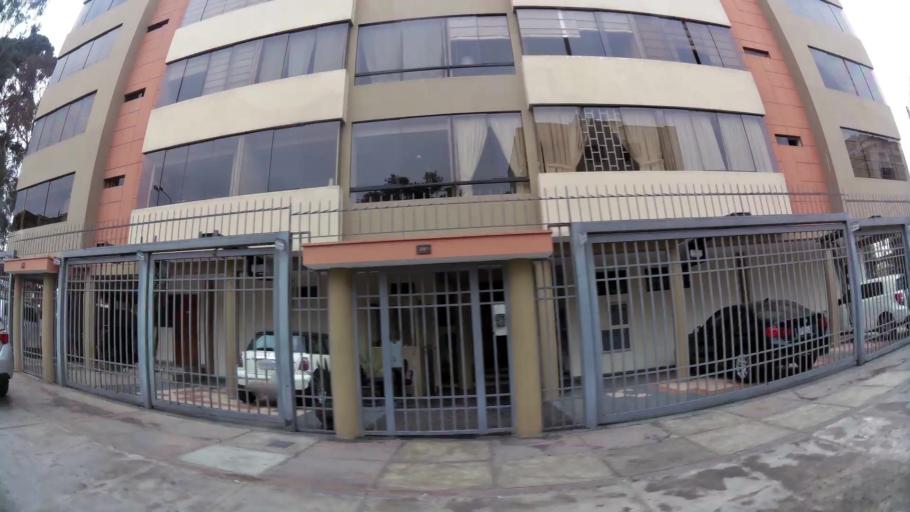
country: PE
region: Lima
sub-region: Lima
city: Surco
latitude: -12.1067
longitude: -77.0089
